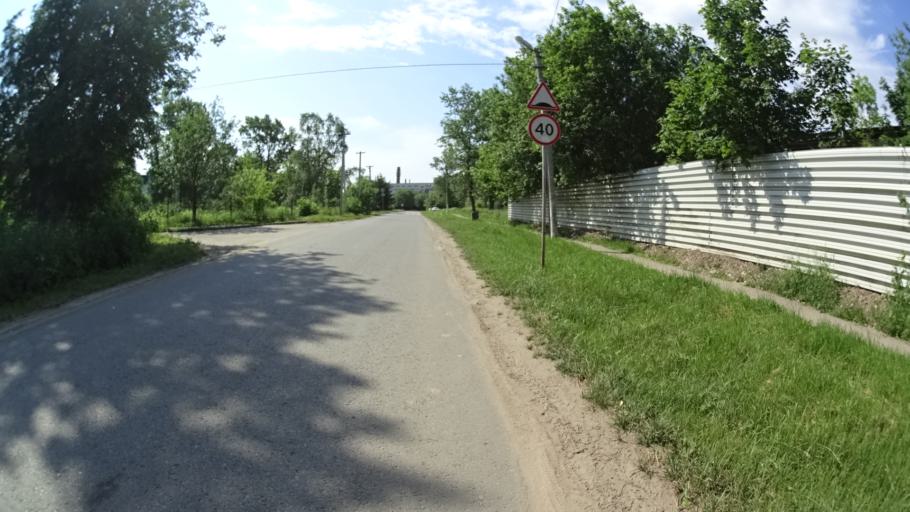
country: RU
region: Moskovskaya
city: Zelenogradskiy
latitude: 56.0866
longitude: 37.9322
